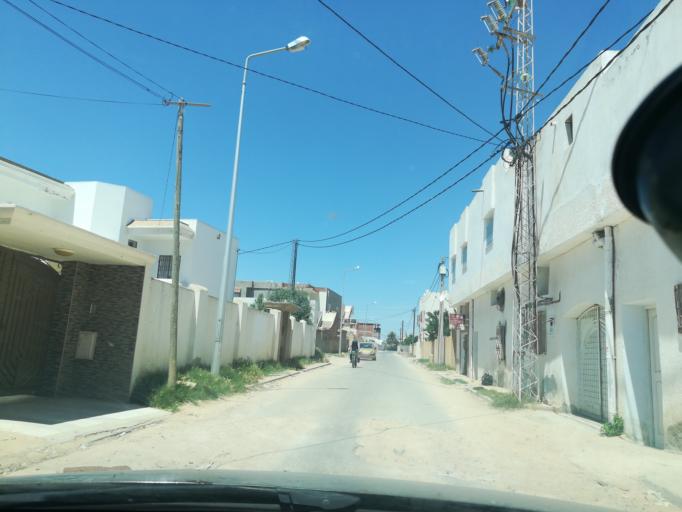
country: TN
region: Safaqis
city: Al Qarmadah
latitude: 34.8184
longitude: 10.7556
